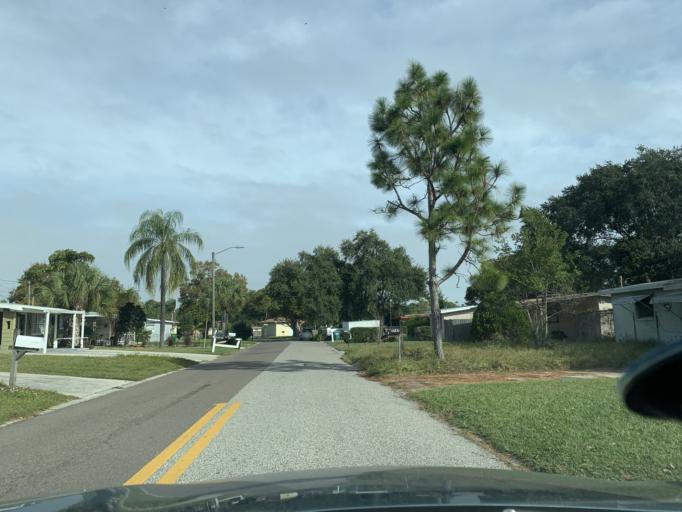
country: US
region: Florida
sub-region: Pinellas County
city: Ridgecrest
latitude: 27.8785
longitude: -82.7825
